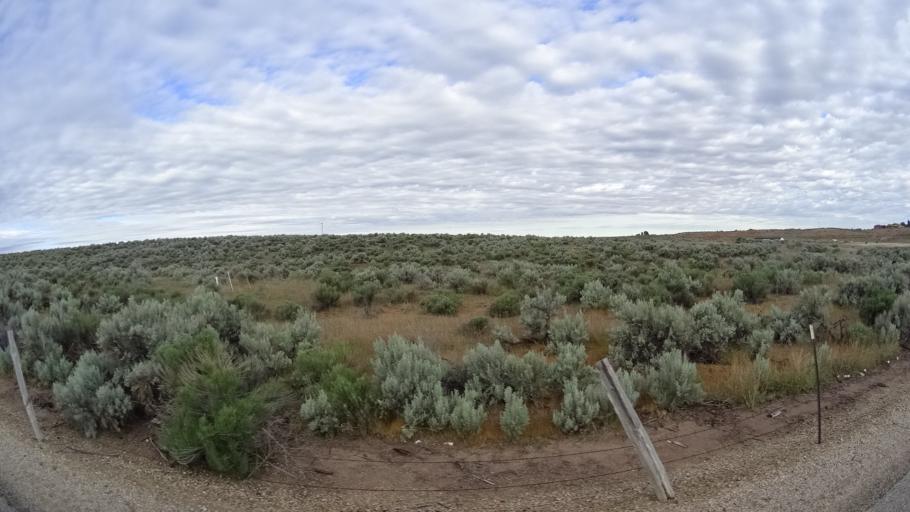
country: US
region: Idaho
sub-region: Ada County
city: Star
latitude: 43.7272
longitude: -116.5127
